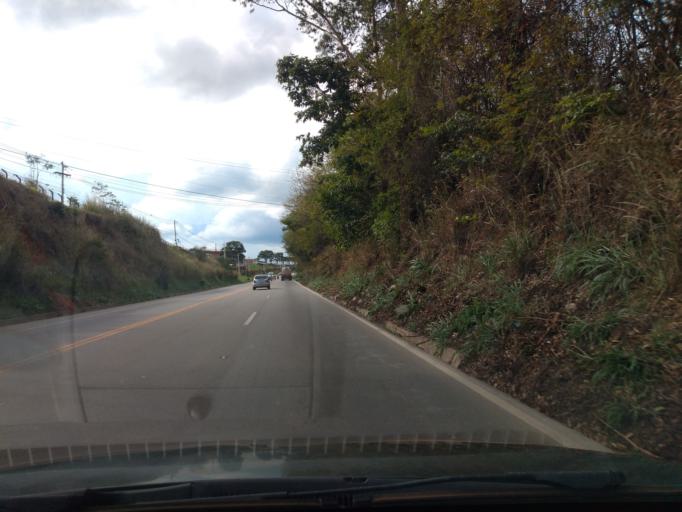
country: BR
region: Minas Gerais
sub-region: Varginha
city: Varginha
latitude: -21.6022
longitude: -45.4362
